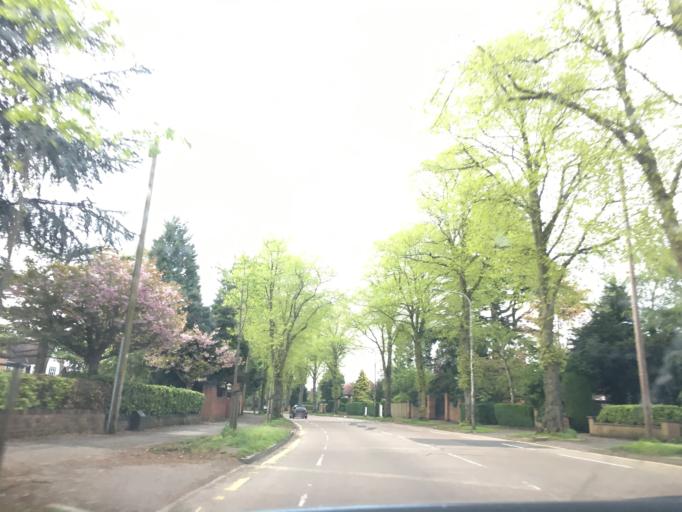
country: GB
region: England
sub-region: Leicestershire
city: Oadby
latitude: 52.6278
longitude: -1.0661
